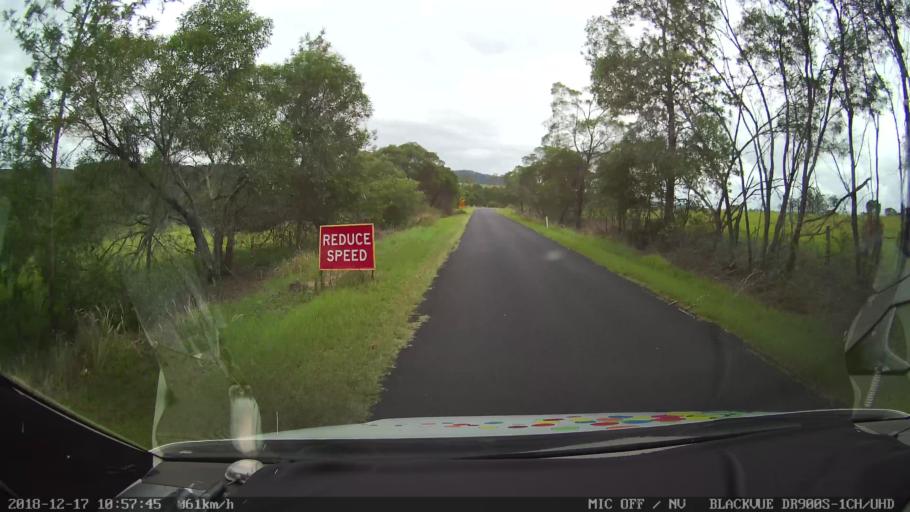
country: AU
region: New South Wales
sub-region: Richmond Valley
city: Casino
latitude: -28.8233
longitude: 152.5992
